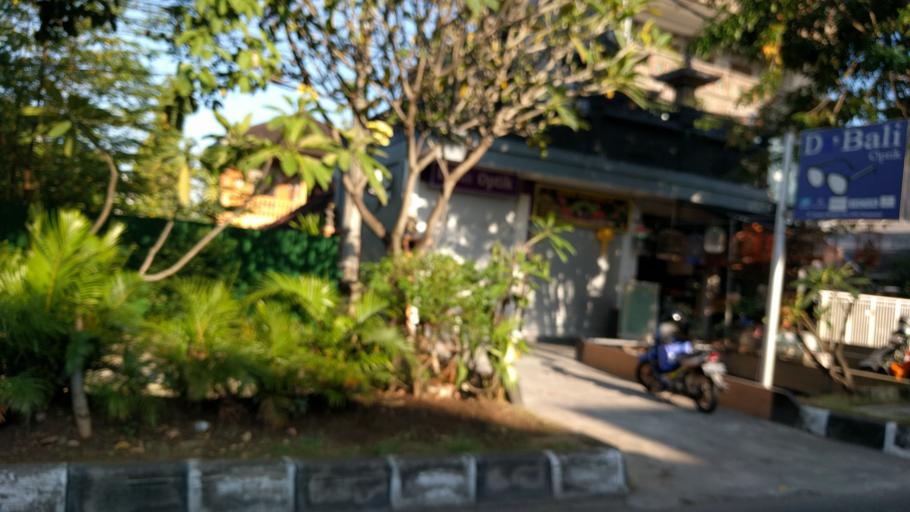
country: ID
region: Bali
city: Kuta
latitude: -8.7032
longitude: 115.1848
